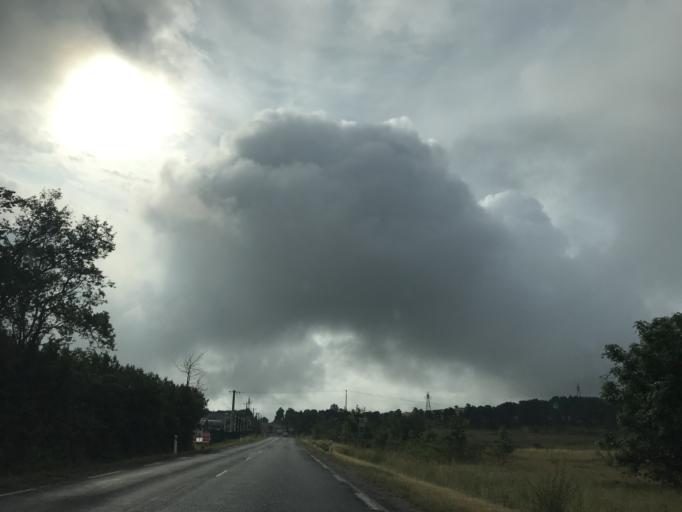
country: FR
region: Auvergne
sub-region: Departement de la Haute-Loire
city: Polignac
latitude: 45.0795
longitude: 3.8310
